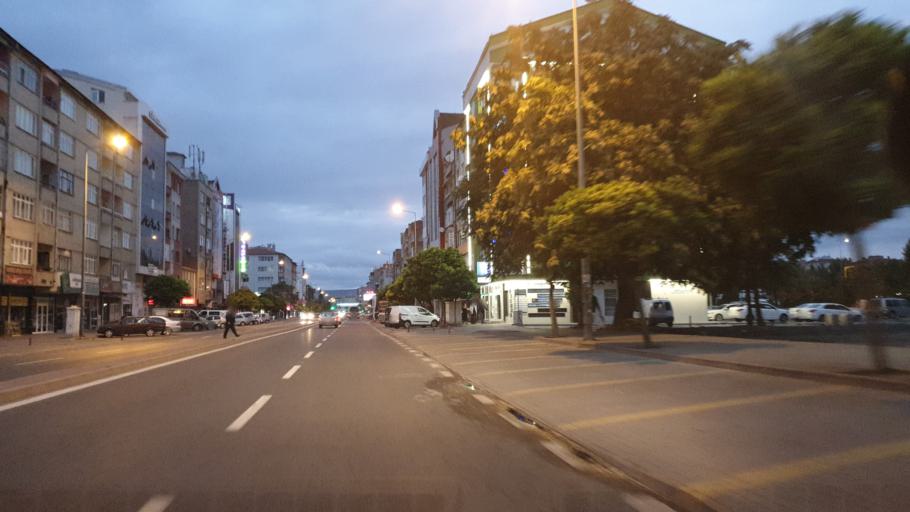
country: TR
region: Kayseri
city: Kayseri
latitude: 38.7236
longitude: 35.4814
